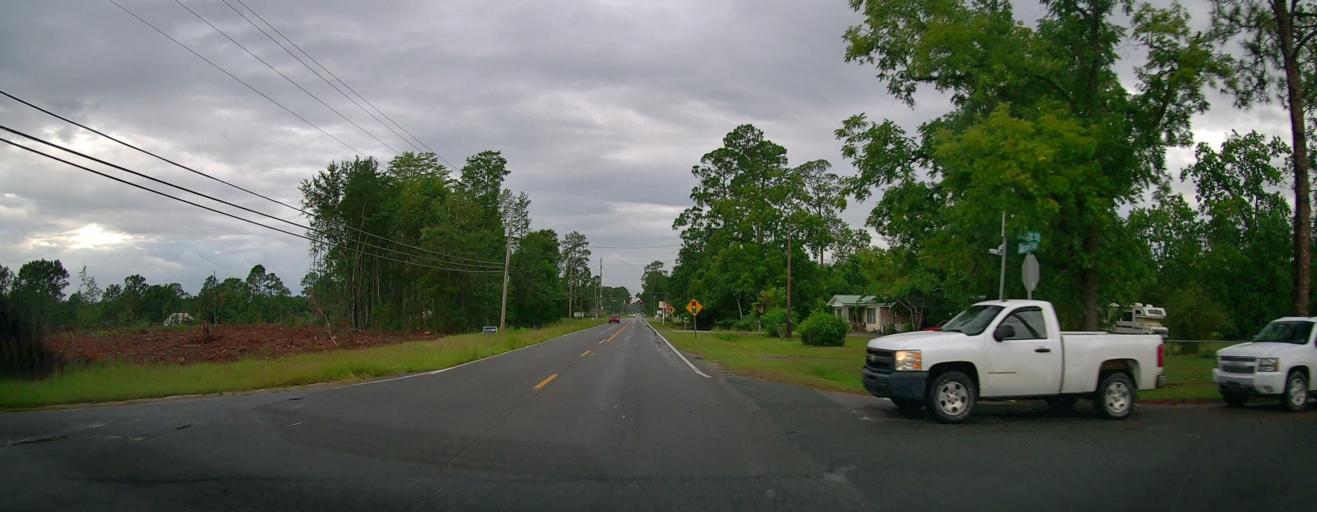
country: US
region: Georgia
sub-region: Ware County
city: Deenwood
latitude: 31.2138
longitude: -82.3857
